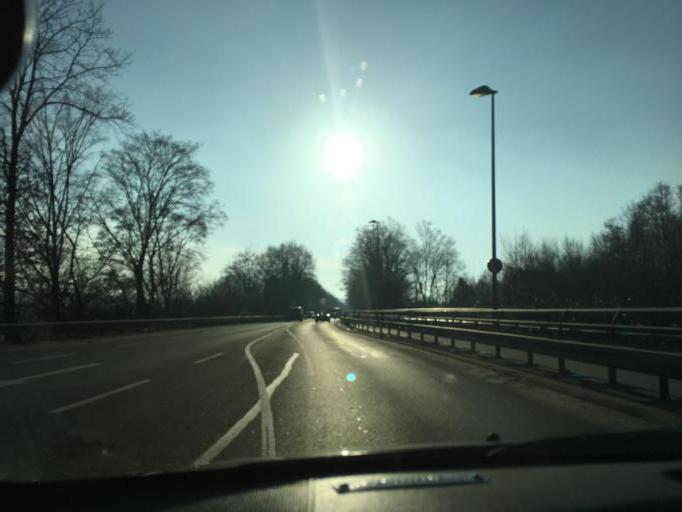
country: DE
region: North Rhine-Westphalia
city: Schwerte
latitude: 51.4426
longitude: 7.5745
